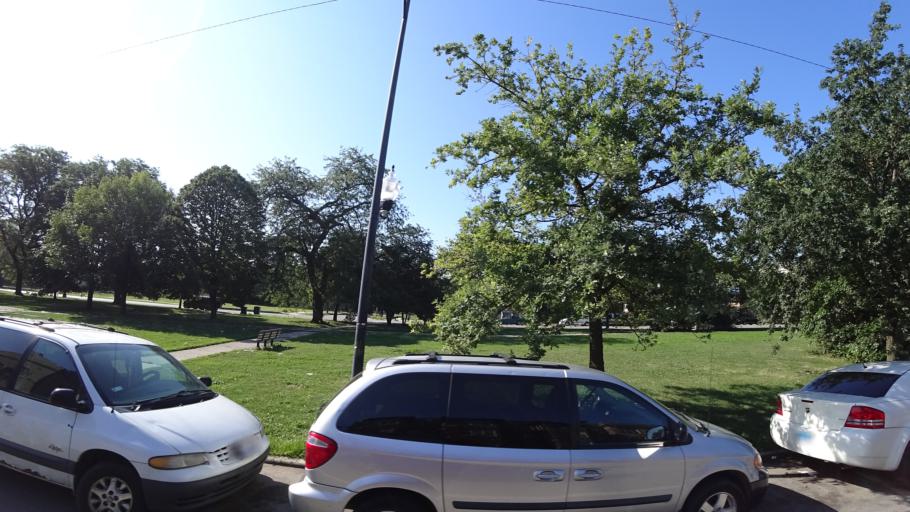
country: US
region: Illinois
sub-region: Cook County
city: Cicero
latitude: 41.8629
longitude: -87.7166
